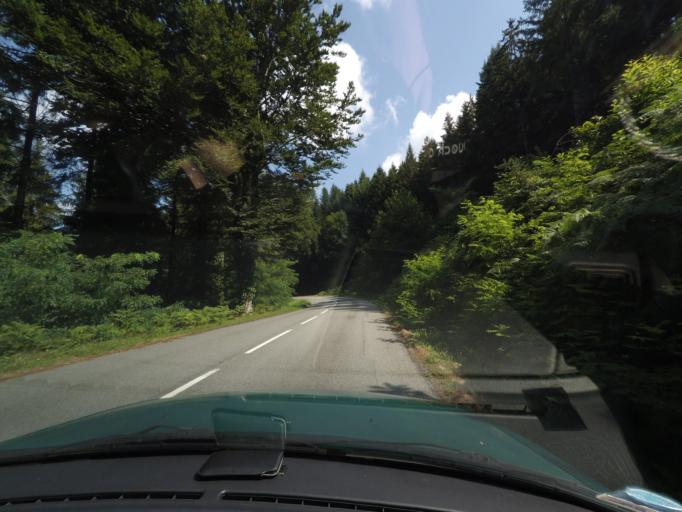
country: FR
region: Limousin
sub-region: Departement de la Haute-Vienne
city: Eymoutiers
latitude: 45.7254
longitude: 1.7871
